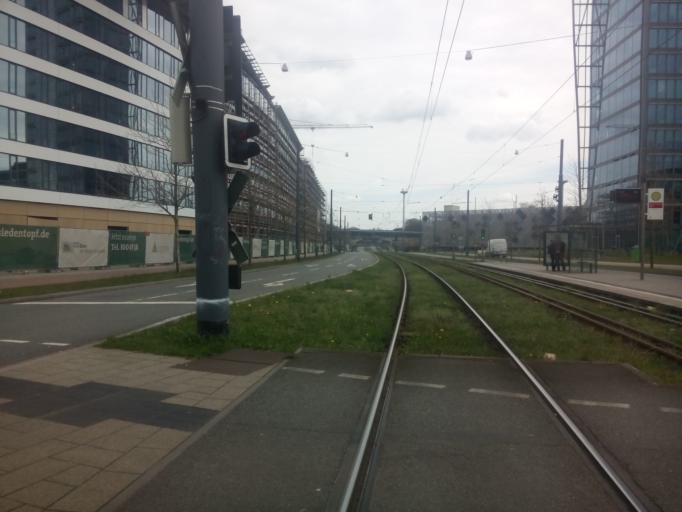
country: DE
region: Bremen
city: Bremen
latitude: 53.0829
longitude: 8.7877
